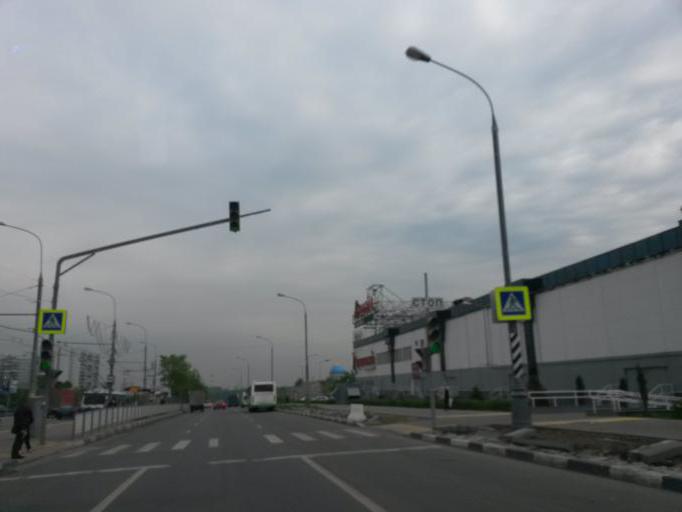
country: RU
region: Moscow
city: Orekhovo-Borisovo
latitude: 55.6213
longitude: 37.7128
